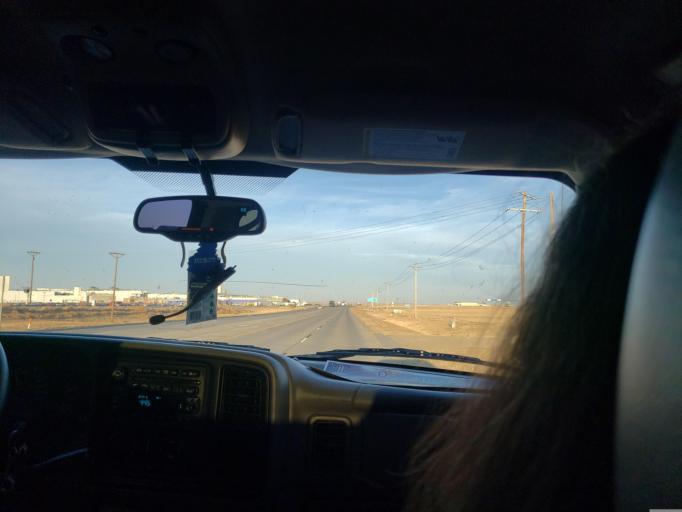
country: US
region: Oklahoma
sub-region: Texas County
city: Guymon
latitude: 36.7037
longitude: -101.4484
